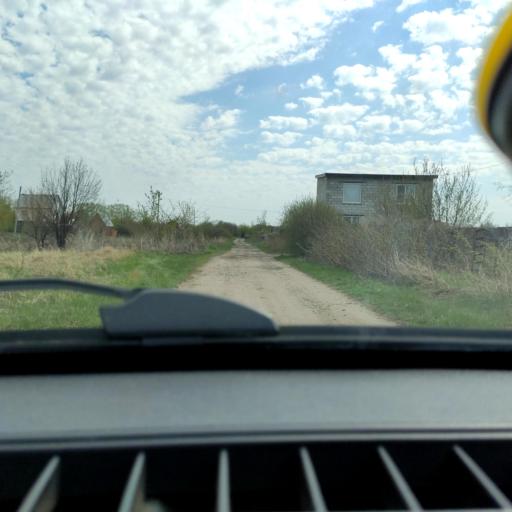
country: RU
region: Samara
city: Tol'yatti
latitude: 53.6977
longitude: 49.4521
